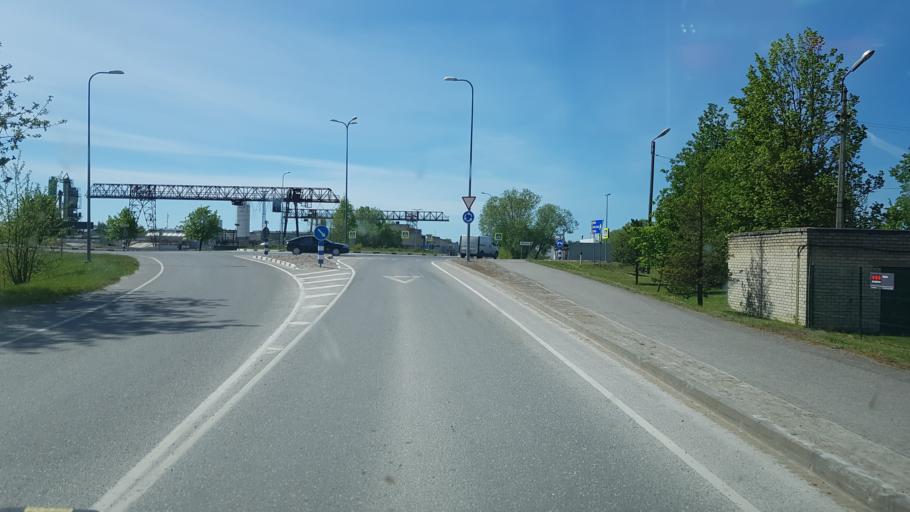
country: EE
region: Saare
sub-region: Kuressaare linn
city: Kuressaare
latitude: 58.2688
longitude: 22.4908
